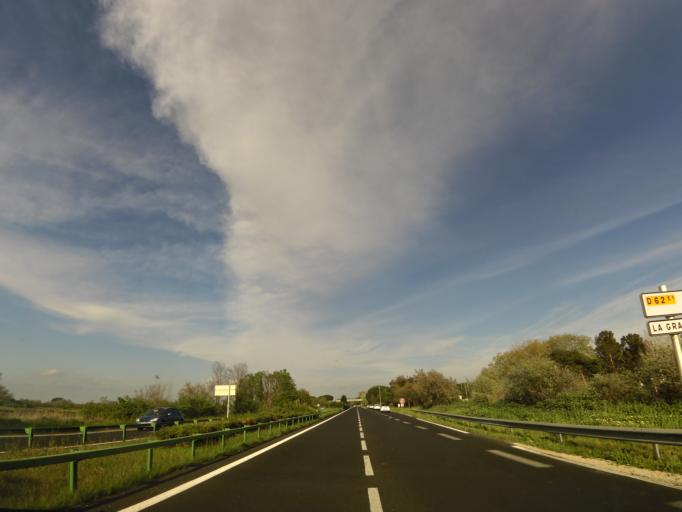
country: FR
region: Languedoc-Roussillon
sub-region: Departement de l'Herault
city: La Grande-Motte
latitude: 43.5696
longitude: 4.0738
